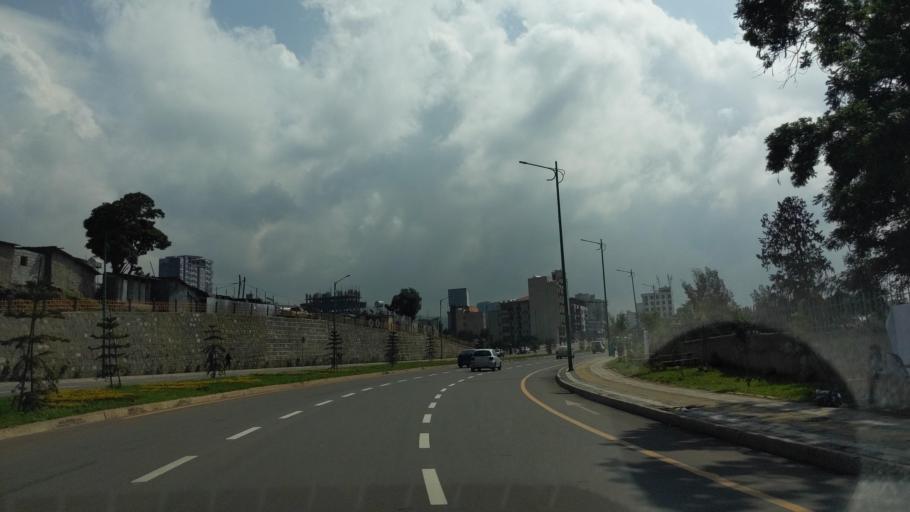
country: ET
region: Adis Abeba
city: Addis Ababa
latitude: 9.0050
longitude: 38.7738
